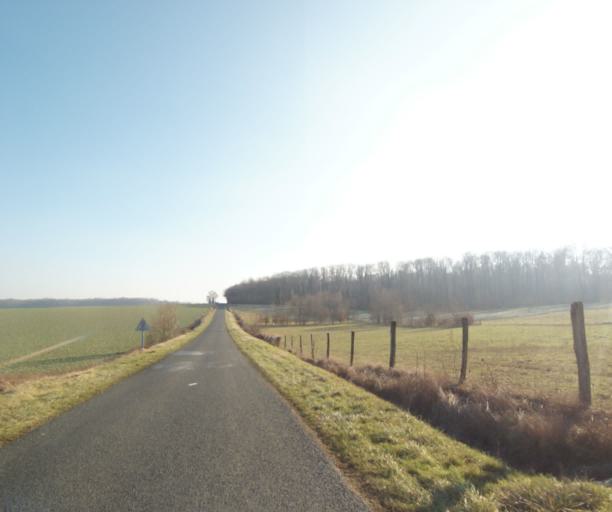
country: FR
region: Champagne-Ardenne
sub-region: Departement de la Haute-Marne
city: Chevillon
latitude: 48.4915
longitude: 5.0743
